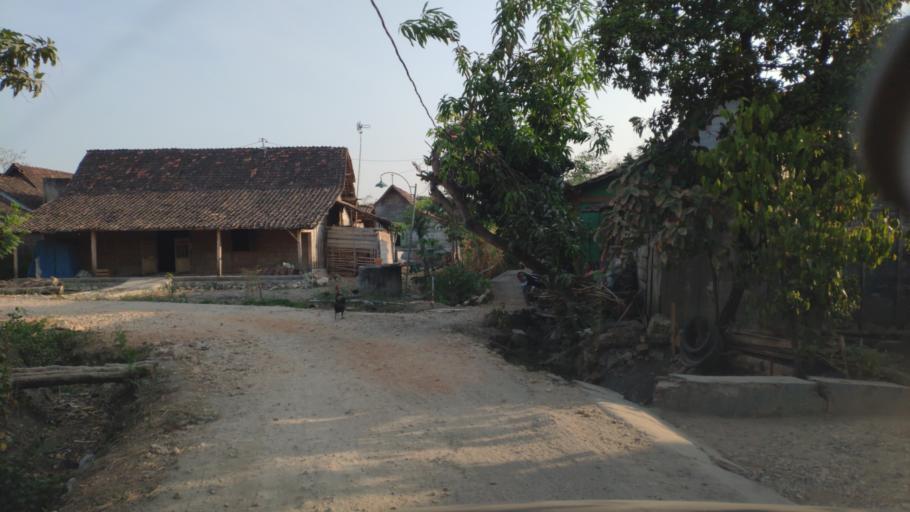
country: ID
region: Central Java
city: Jepang Satu
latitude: -7.0184
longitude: 111.4252
